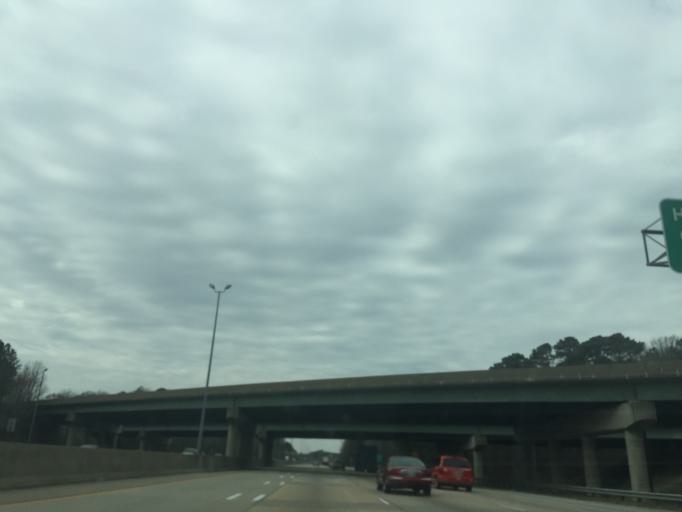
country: US
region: Virginia
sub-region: City of Hampton
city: Hampton
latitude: 37.0586
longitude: -76.4165
